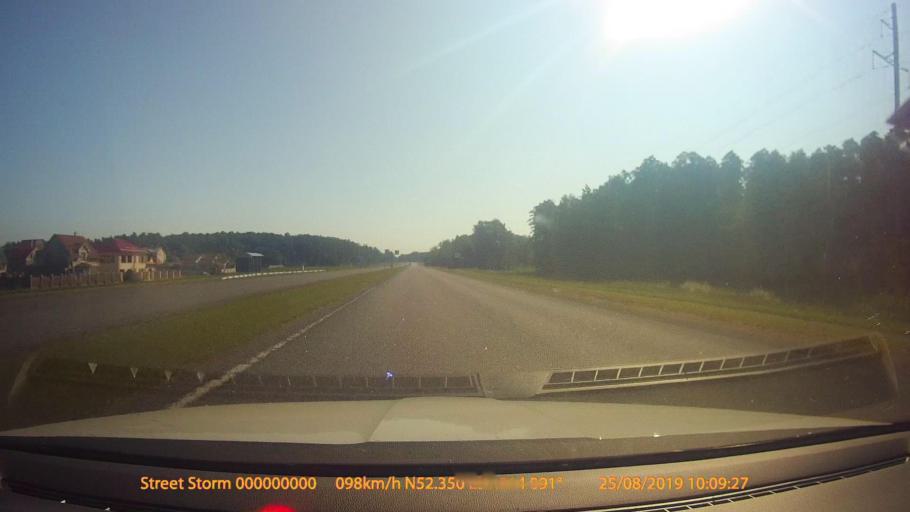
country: BY
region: Gomel
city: Gomel
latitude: 52.3504
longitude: 31.0154
